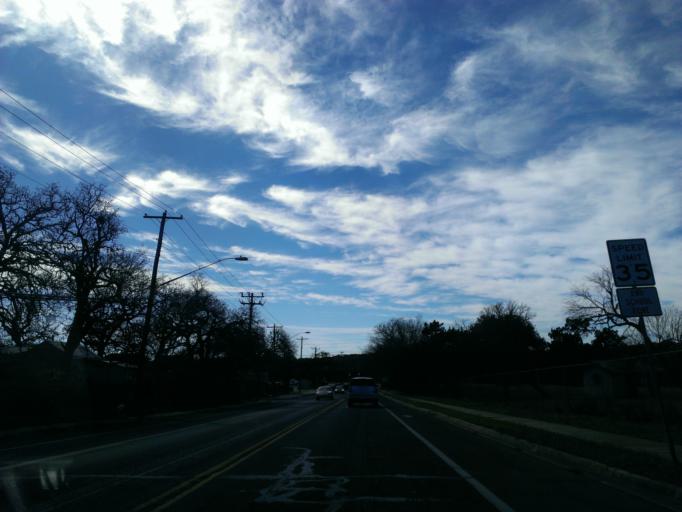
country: US
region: Texas
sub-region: Travis County
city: Rollingwood
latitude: 30.2850
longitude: -97.7756
